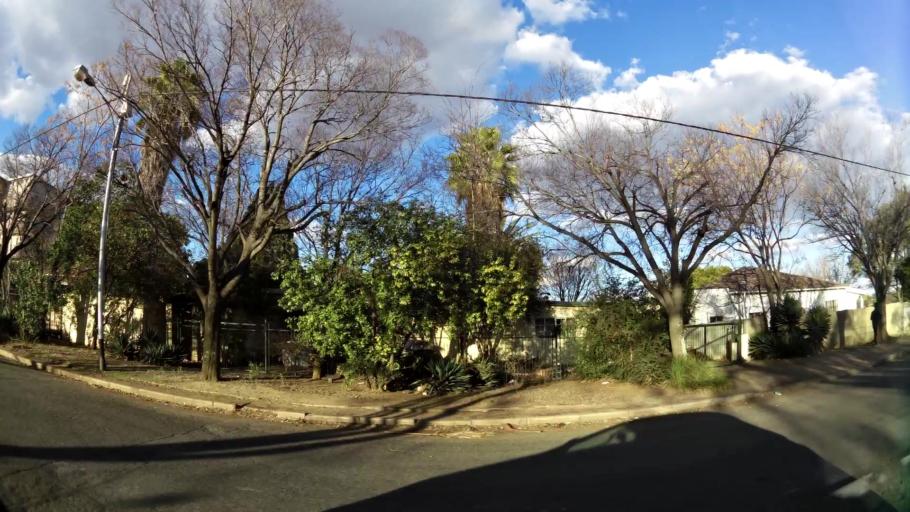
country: ZA
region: North-West
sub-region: Dr Kenneth Kaunda District Municipality
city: Potchefstroom
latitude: -26.7018
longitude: 27.0887
